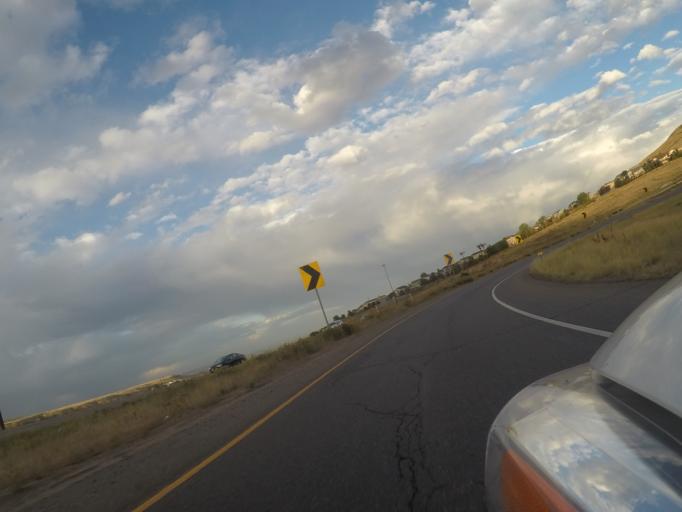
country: US
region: Colorado
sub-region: Jefferson County
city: West Pleasant View
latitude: 39.7154
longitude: -105.1944
